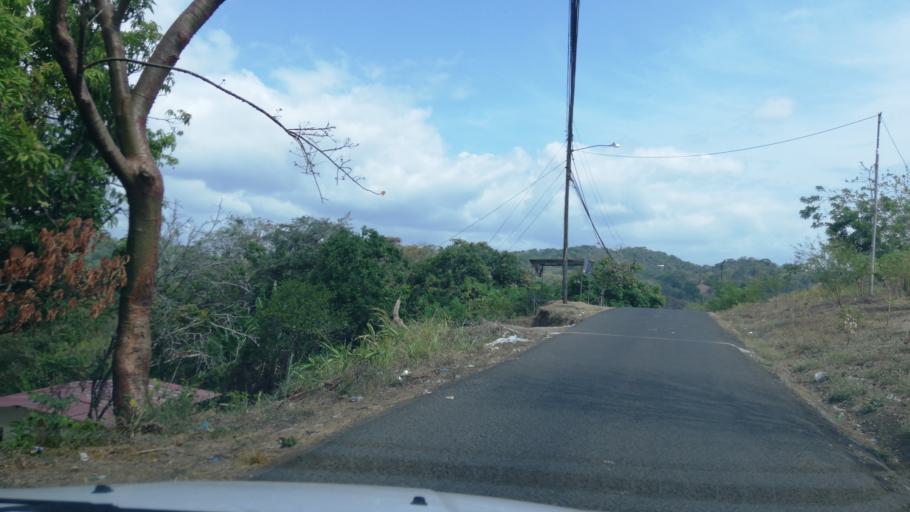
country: PA
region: Panama
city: Alcalde Diaz
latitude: 9.1247
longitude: -79.5640
